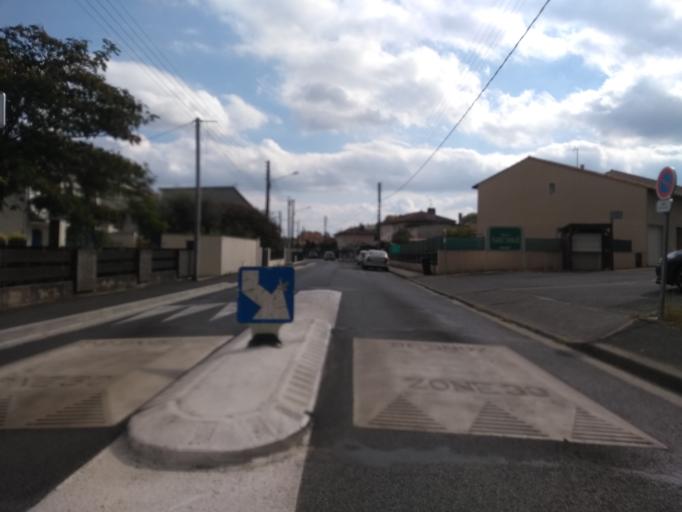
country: FR
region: Aquitaine
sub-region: Departement de la Gironde
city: Begles
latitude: 44.7967
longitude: -0.5625
